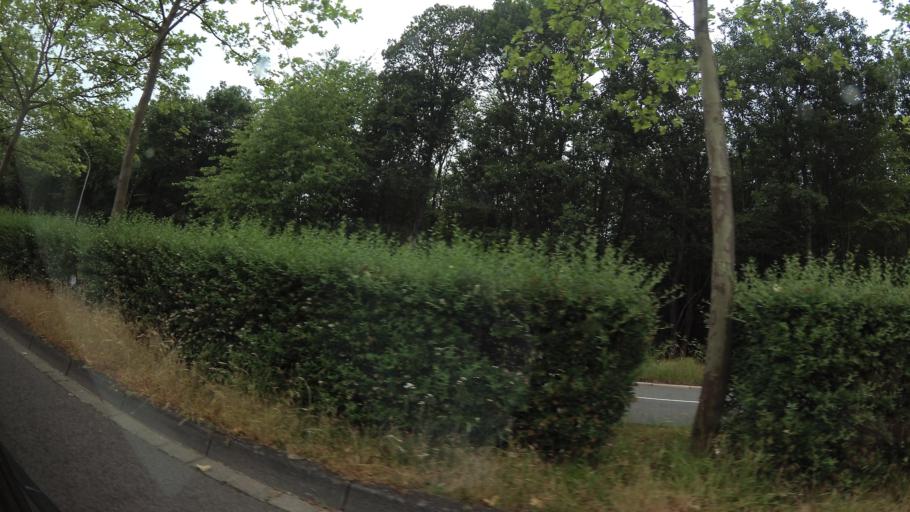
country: DE
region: Saarland
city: Saarbrucken
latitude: 49.2568
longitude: 6.9565
